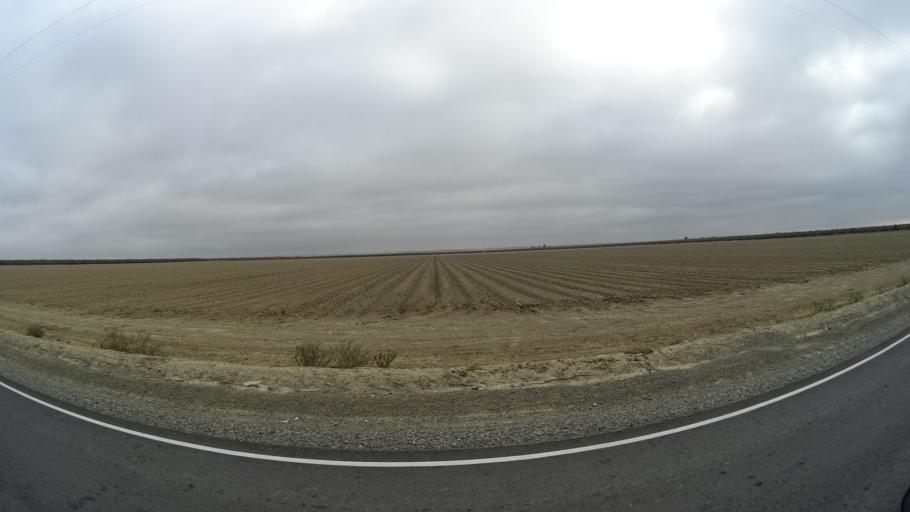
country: US
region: California
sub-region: Yolo County
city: Esparto
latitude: 38.7698
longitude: -122.0440
